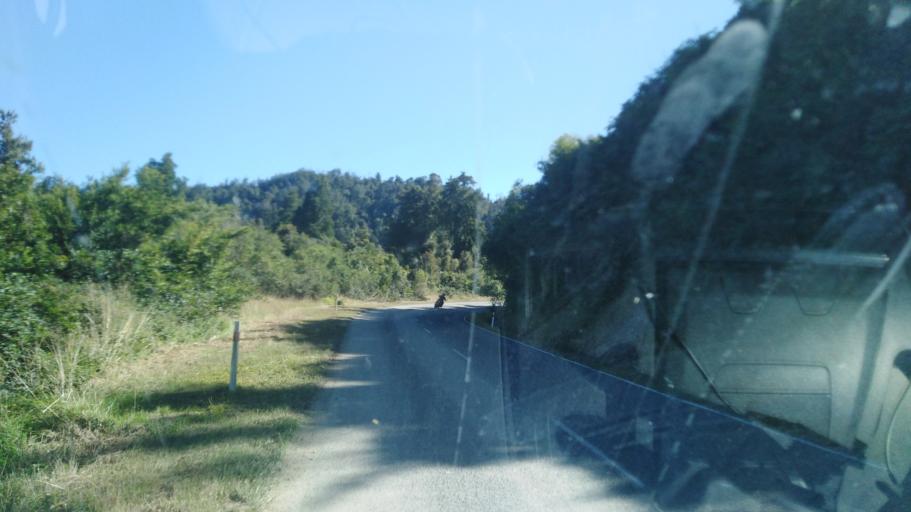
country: NZ
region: West Coast
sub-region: Buller District
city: Westport
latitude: -41.5306
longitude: 171.9938
